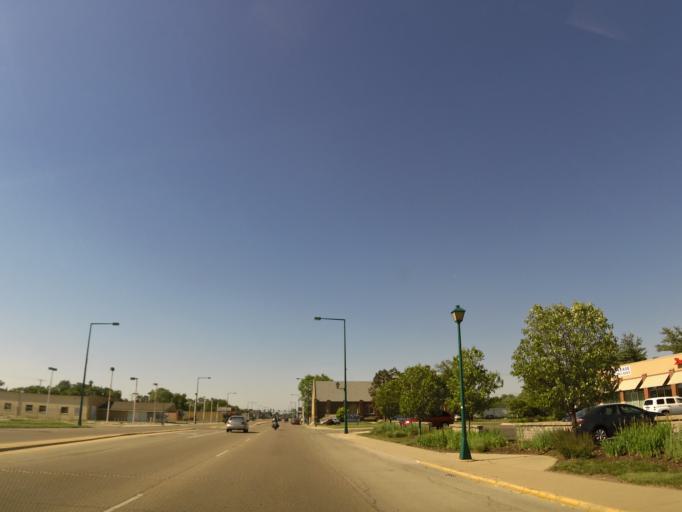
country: US
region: Illinois
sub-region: Winnebago County
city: Loves Park
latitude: 42.3078
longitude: -89.0577
